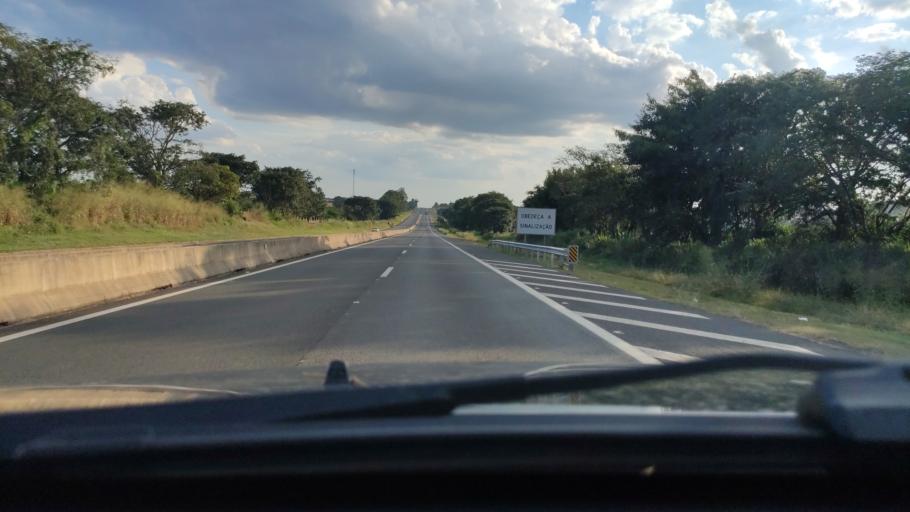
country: BR
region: Sao Paulo
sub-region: Artur Nogueira
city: Artur Nogueira
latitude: -22.4581
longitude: -47.0968
